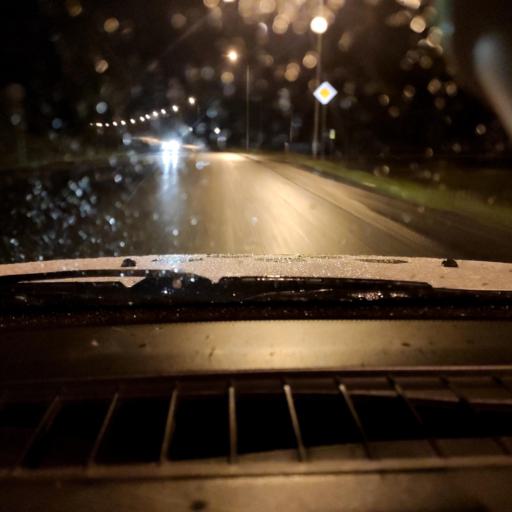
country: RU
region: Udmurtiya
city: Khokhryaki
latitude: 57.1737
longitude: 53.1590
